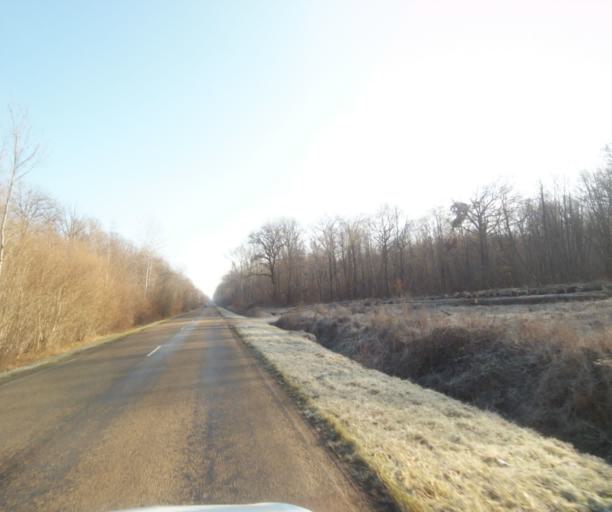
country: FR
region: Champagne-Ardenne
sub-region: Departement de la Haute-Marne
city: Laneuville-a-Remy
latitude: 48.4929
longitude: 4.8905
